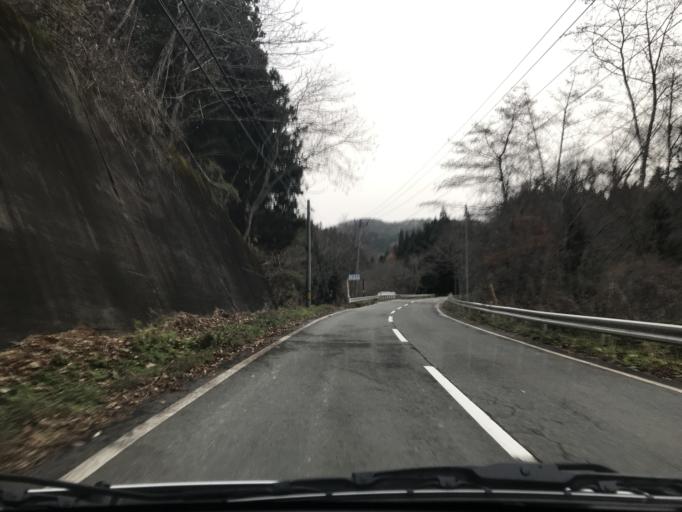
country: JP
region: Iwate
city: Tono
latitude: 39.1812
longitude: 141.3614
